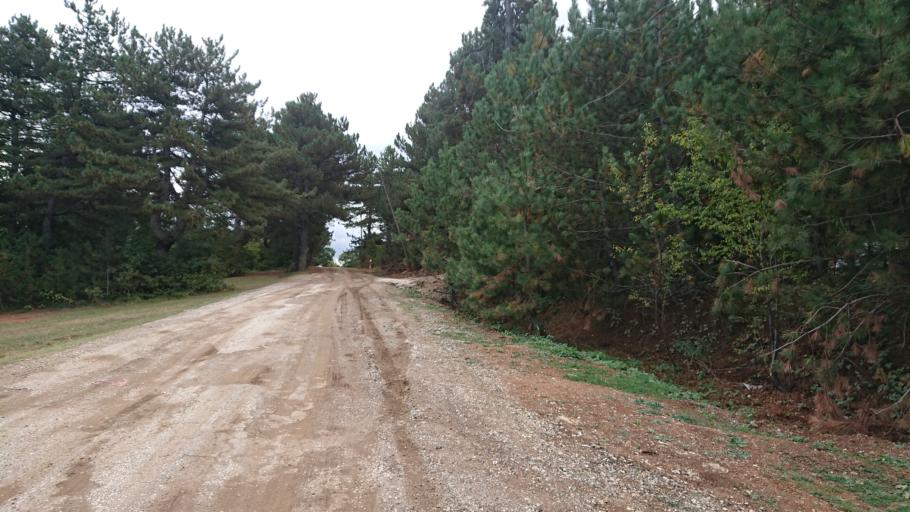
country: TR
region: Bilecik
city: Pazaryeri
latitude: 40.0150
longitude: 29.7970
